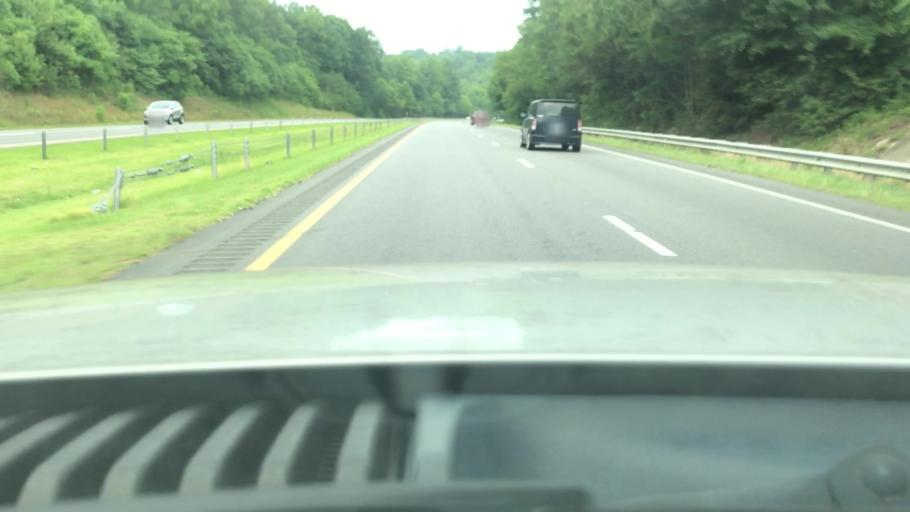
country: US
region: North Carolina
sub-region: Wilkes County
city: North Wilkesboro
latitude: 36.1329
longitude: -81.1283
